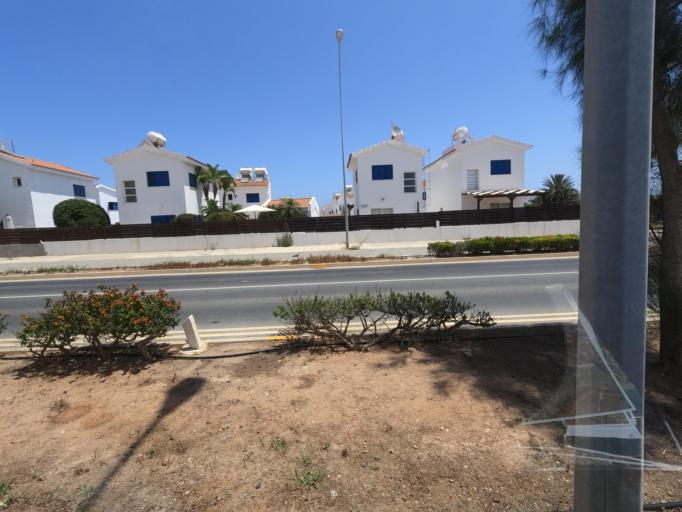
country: CY
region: Ammochostos
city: Protaras
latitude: 35.0334
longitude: 34.0272
